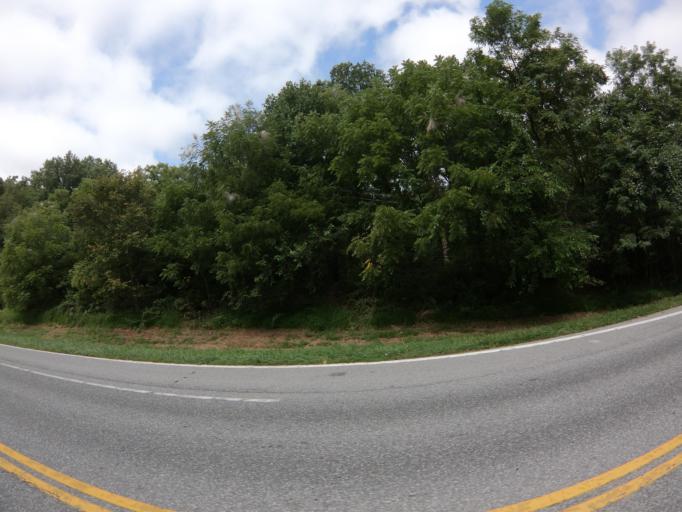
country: US
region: Maryland
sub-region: Howard County
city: Highland
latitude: 39.2282
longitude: -76.9181
